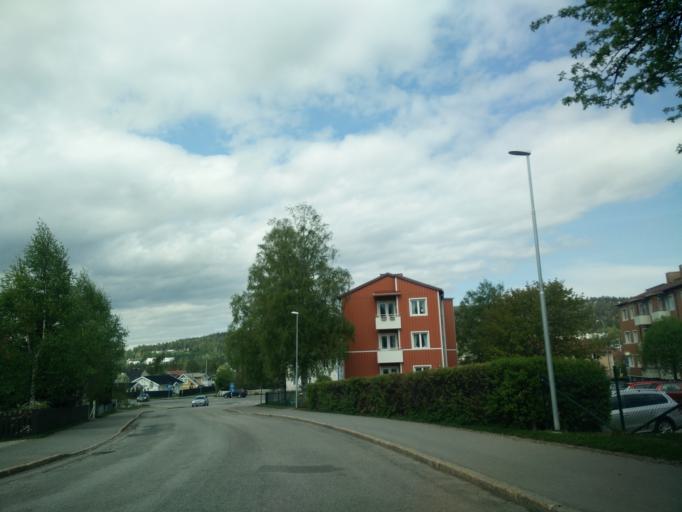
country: SE
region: Vaesternorrland
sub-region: Sundsvalls Kommun
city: Sundsvall
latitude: 62.3877
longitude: 17.2830
